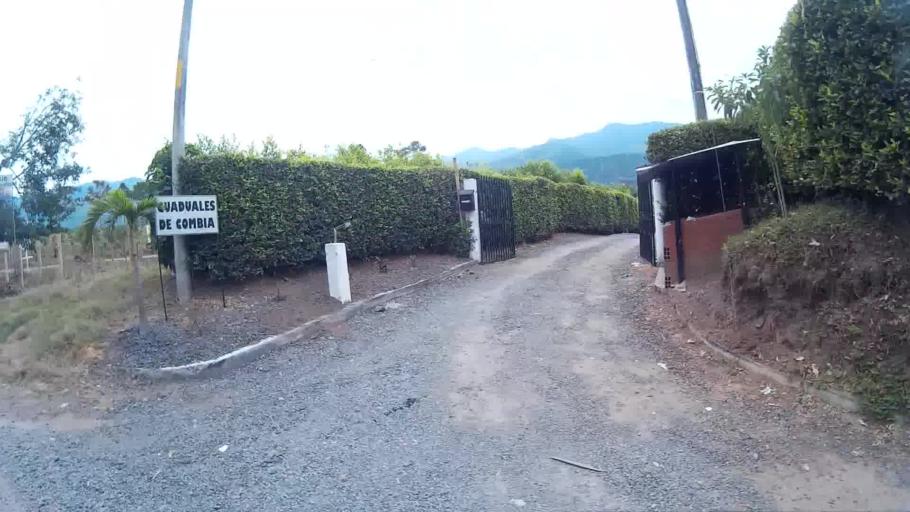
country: CO
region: Risaralda
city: Pereira
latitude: 4.8345
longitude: -75.7569
